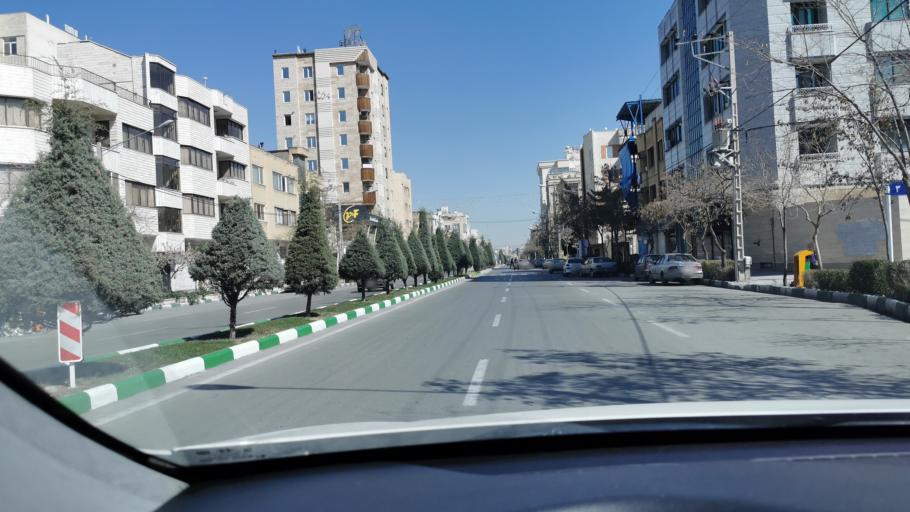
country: IR
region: Razavi Khorasan
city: Mashhad
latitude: 36.3214
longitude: 59.5252
